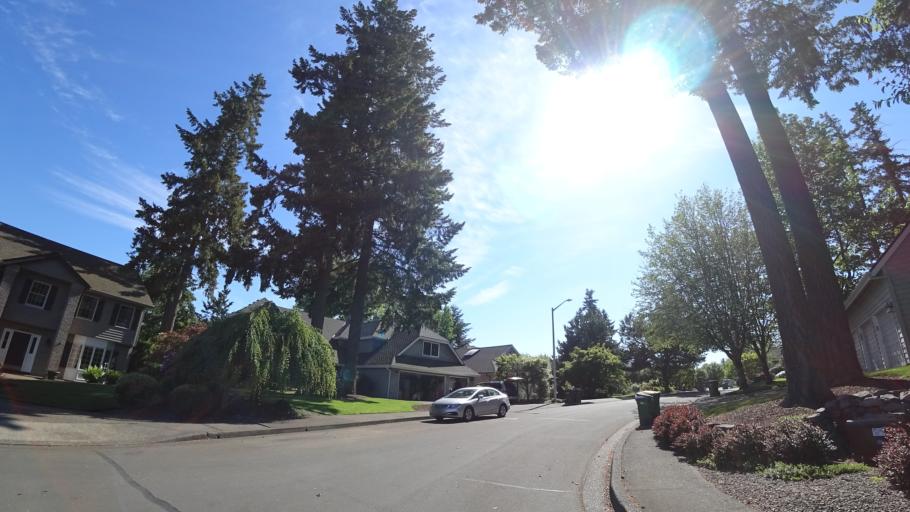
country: US
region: Oregon
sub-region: Washington County
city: Beaverton
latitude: 45.4453
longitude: -122.8165
